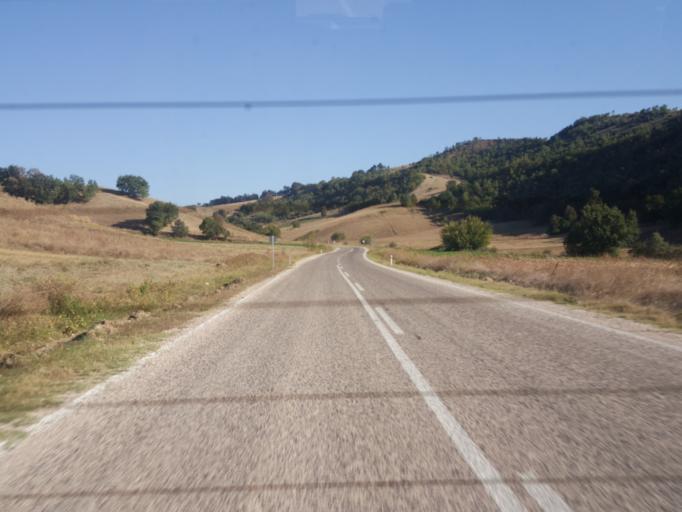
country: TR
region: Amasya
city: Tasova
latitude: 40.7208
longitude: 36.3032
